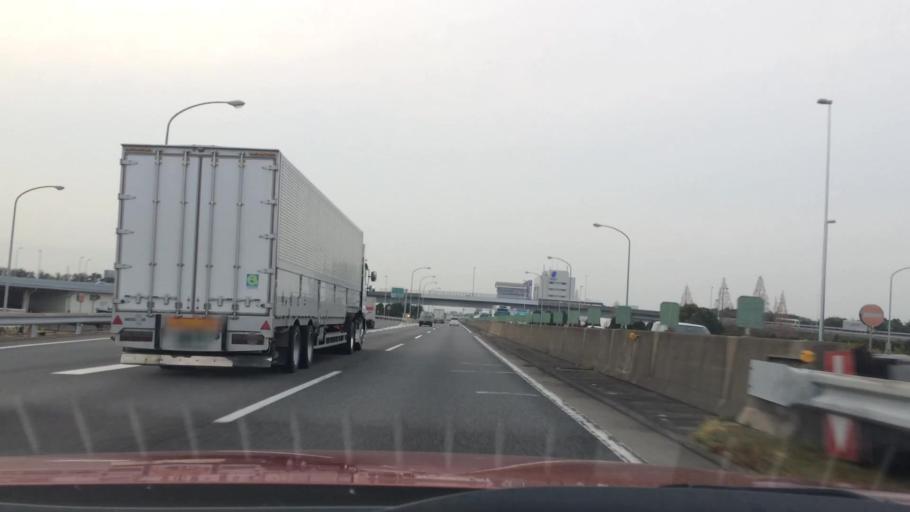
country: JP
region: Aichi
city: Sobue
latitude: 35.3068
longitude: 136.6943
